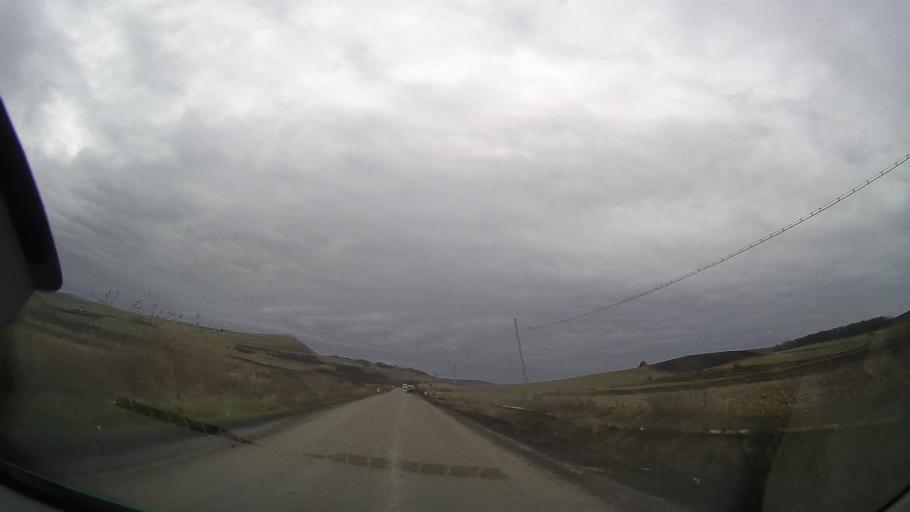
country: RO
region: Cluj
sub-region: Comuna Catina
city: Catina
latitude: 46.8158
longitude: 24.2246
